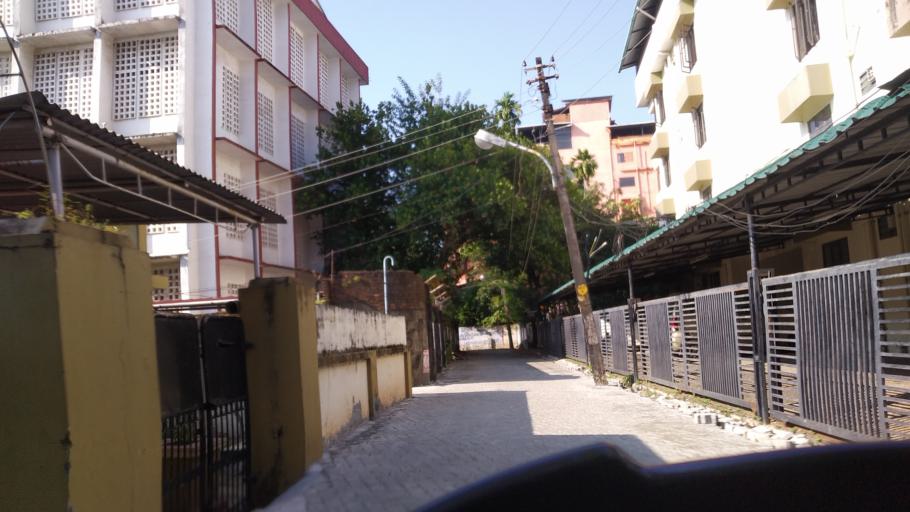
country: IN
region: Kerala
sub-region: Ernakulam
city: Cochin
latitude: 9.9837
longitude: 76.2801
